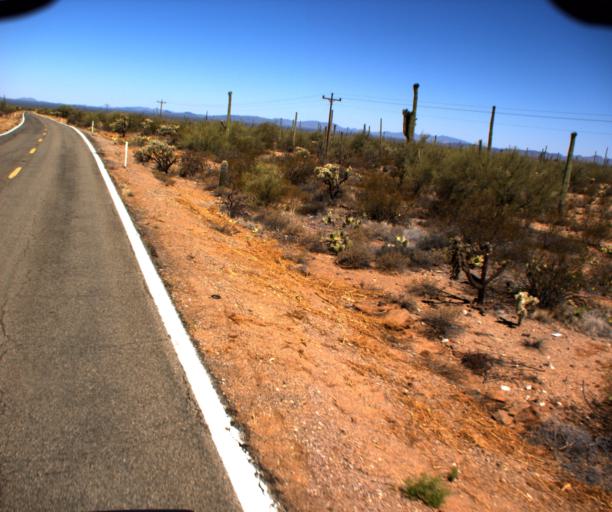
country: US
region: Arizona
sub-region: Pima County
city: Sells
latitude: 32.1768
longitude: -112.2642
